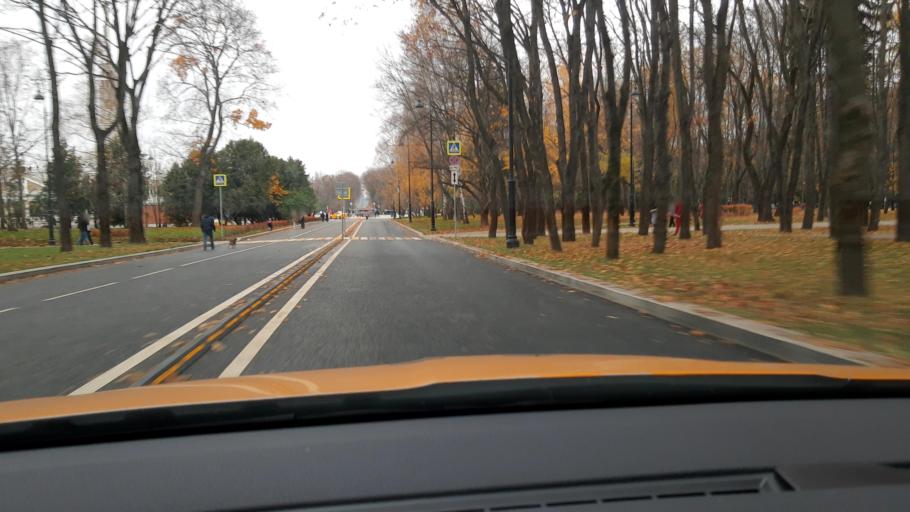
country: RU
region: Moskovskaya
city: Levoberezhnyy
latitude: 55.8494
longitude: 37.4693
